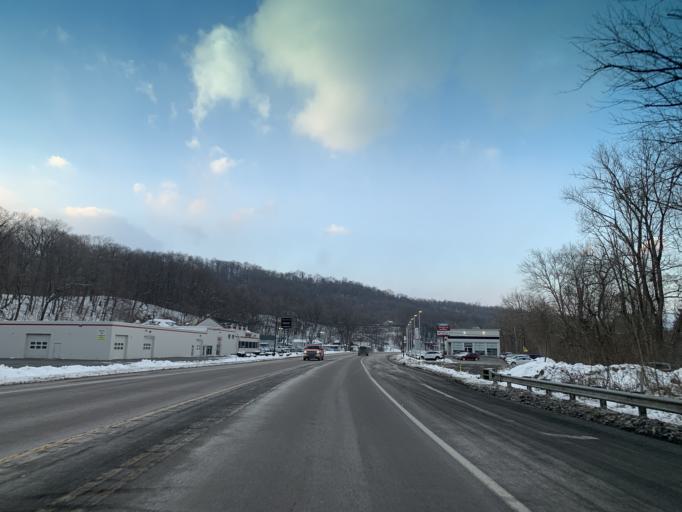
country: US
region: Maryland
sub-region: Allegany County
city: La Vale
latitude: 39.6712
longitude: -78.7910
